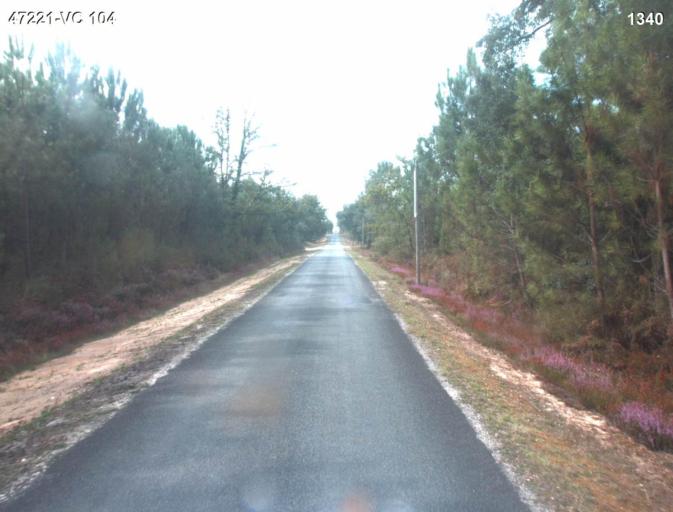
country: FR
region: Aquitaine
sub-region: Departement du Lot-et-Garonne
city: Mezin
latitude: 44.1251
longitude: 0.2119
